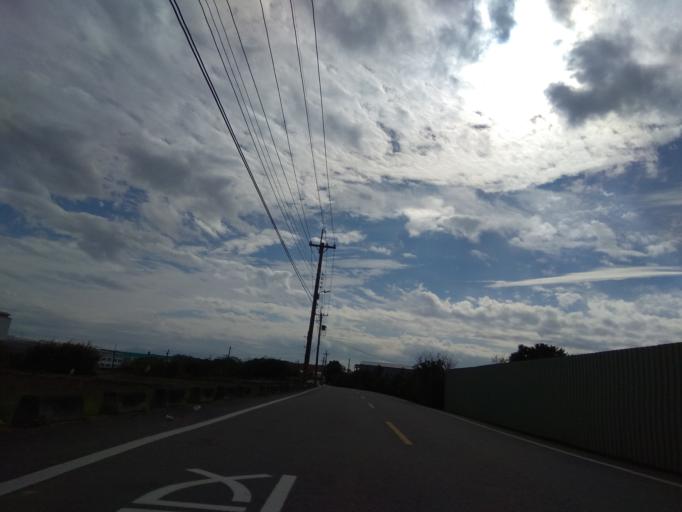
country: TW
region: Taiwan
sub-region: Hsinchu
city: Zhubei
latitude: 24.9583
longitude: 121.1079
